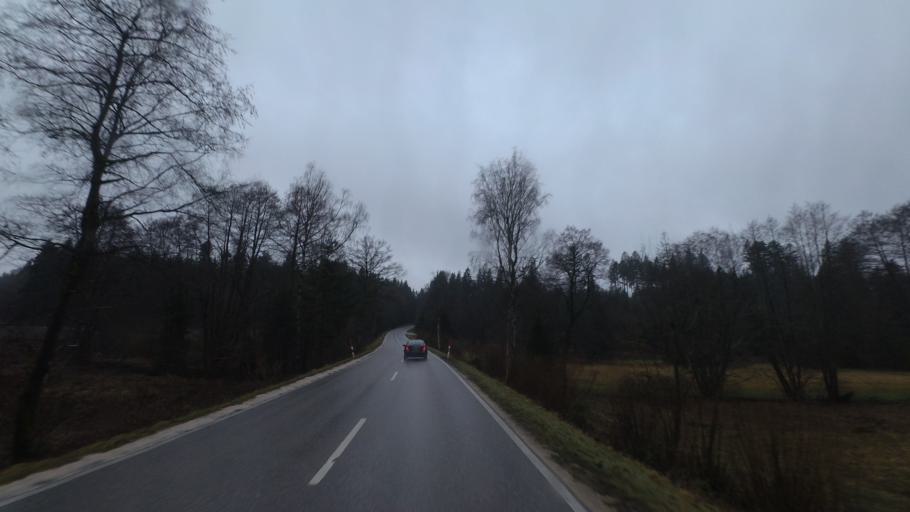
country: DE
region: Bavaria
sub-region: Upper Bavaria
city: Surberg
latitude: 47.8924
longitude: 12.6841
